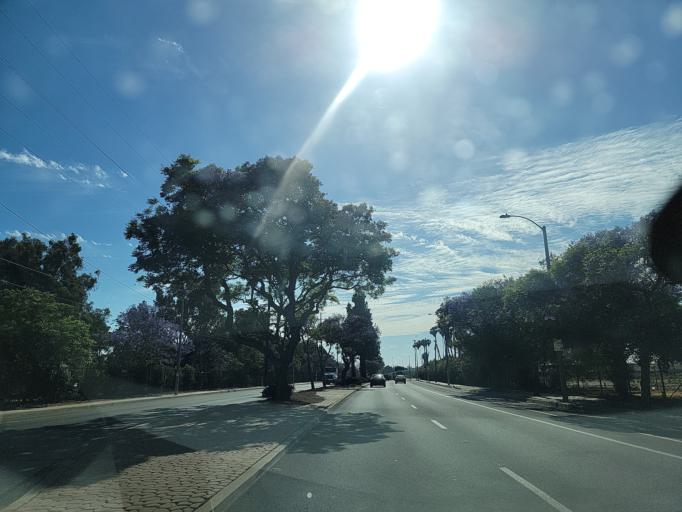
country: US
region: California
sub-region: Los Angeles County
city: West Carson
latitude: 33.8080
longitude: -118.2767
